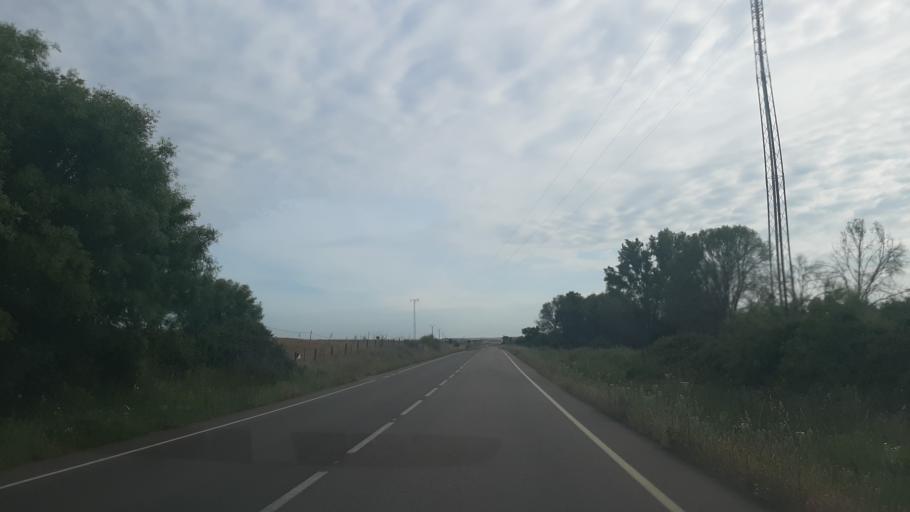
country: ES
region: Castille and Leon
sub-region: Provincia de Salamanca
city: Gallegos de Arganan
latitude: 40.6099
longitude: -6.7066
